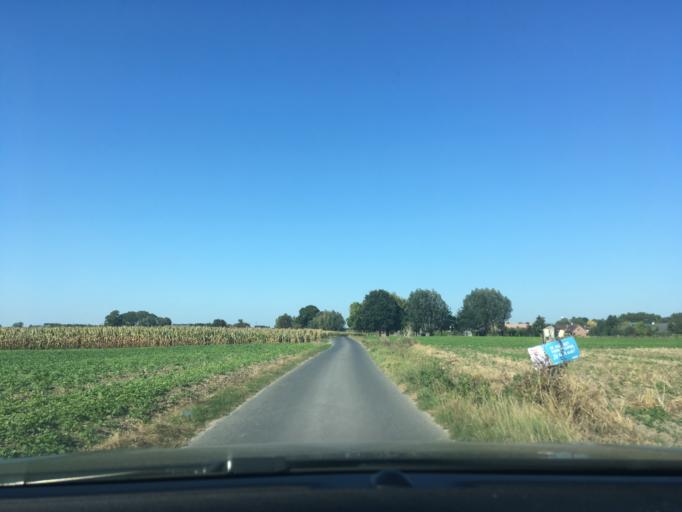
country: BE
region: Flanders
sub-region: Provincie West-Vlaanderen
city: Roeselare
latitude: 50.9062
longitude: 3.1573
